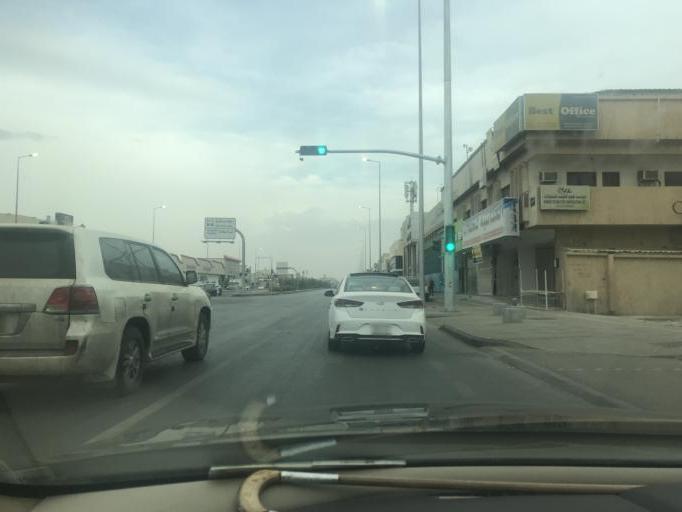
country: SA
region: Ar Riyad
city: Riyadh
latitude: 24.7473
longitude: 46.7741
